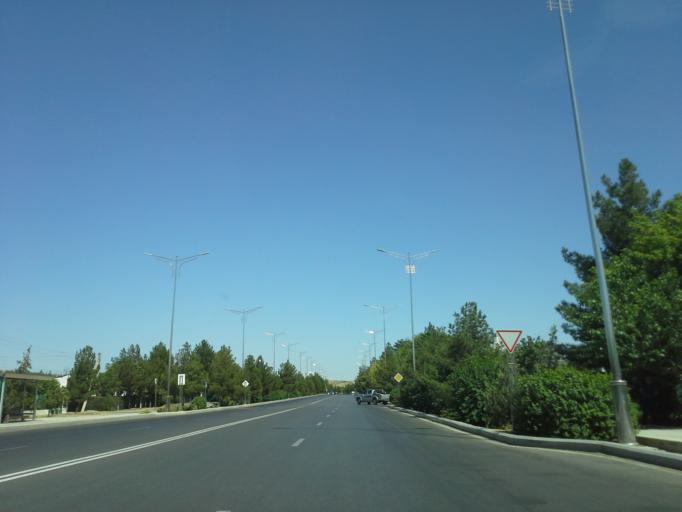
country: TM
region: Ahal
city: Ashgabat
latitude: 37.9307
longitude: 58.2956
